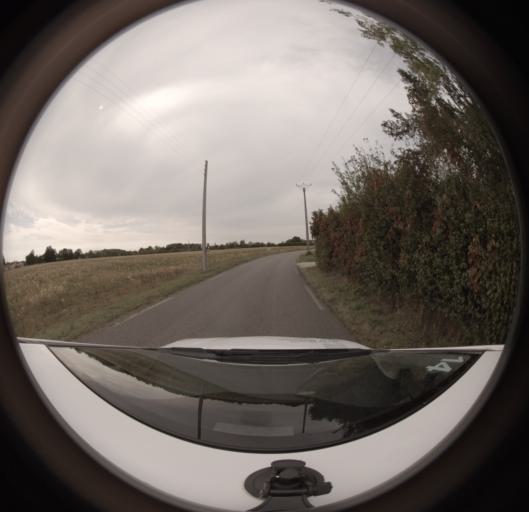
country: FR
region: Midi-Pyrenees
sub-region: Departement du Tarn-et-Garonne
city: Montauban
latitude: 44.0612
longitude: 1.3480
